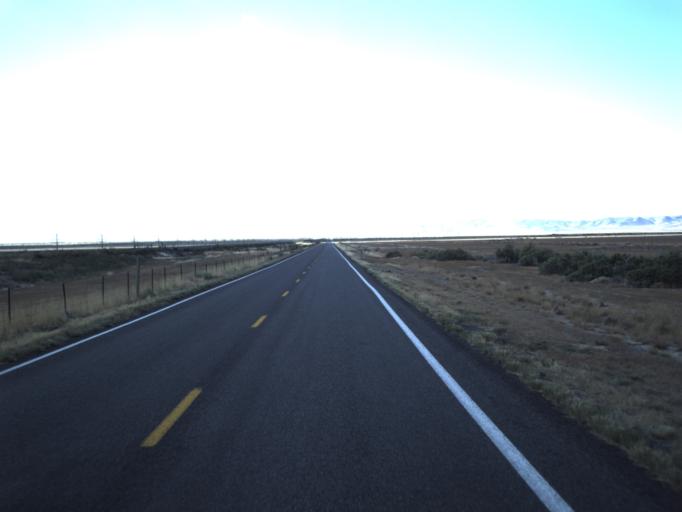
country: US
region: Utah
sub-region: Millard County
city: Delta
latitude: 38.9797
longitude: -112.7957
